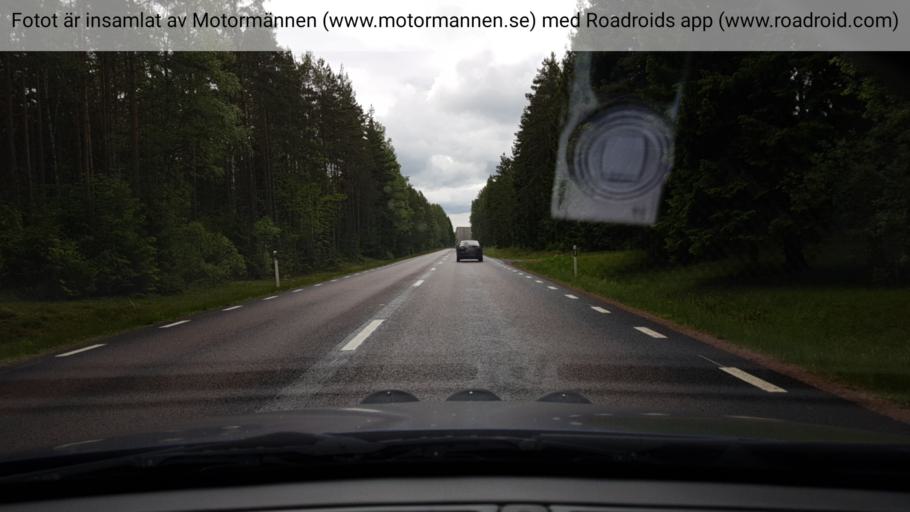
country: SE
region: Vaermland
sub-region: Kristinehamns Kommun
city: Bjorneborg
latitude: 59.2280
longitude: 14.1820
